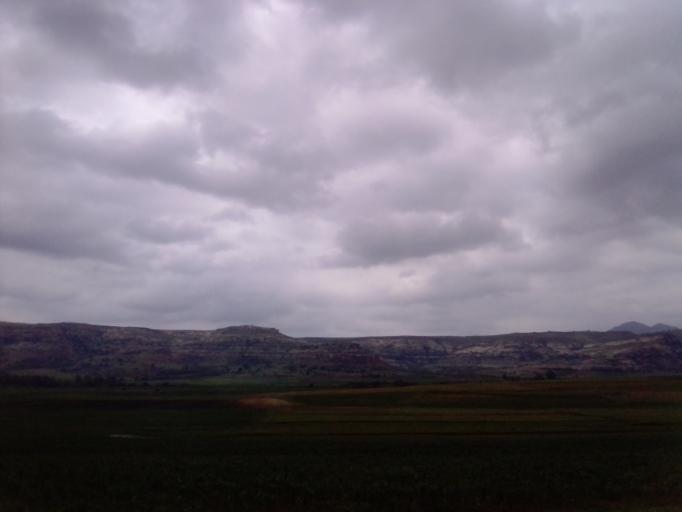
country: LS
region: Leribe
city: Leribe
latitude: -29.0214
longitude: 28.0192
